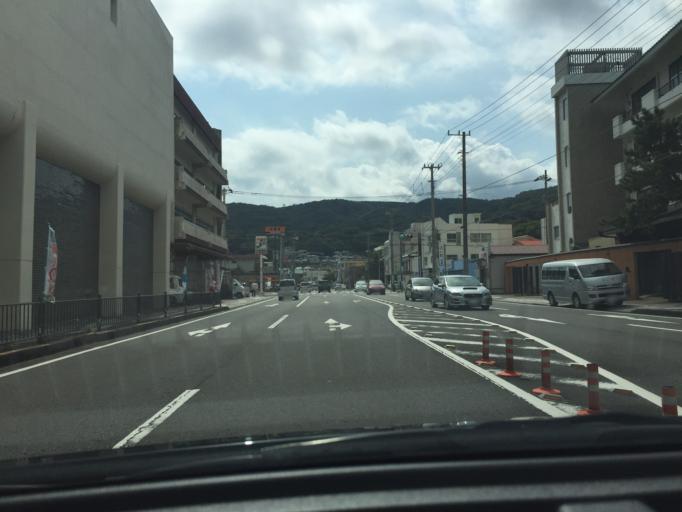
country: JP
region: Shizuoka
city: Ito
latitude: 34.9713
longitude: 139.1020
